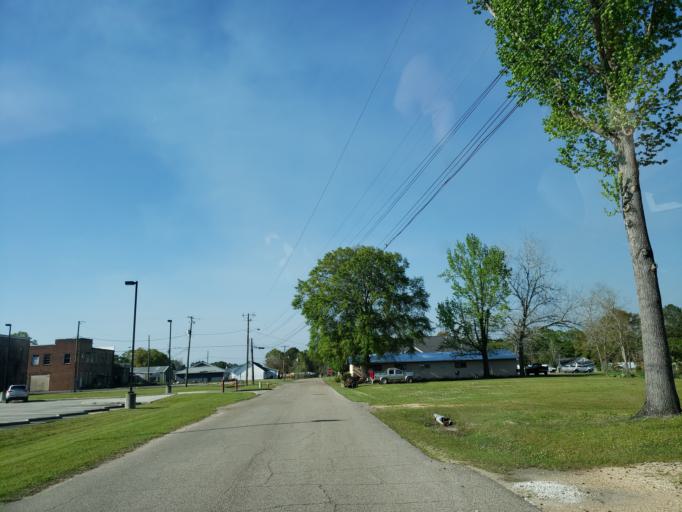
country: US
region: Mississippi
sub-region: Perry County
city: Richton
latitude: 31.3480
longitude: -88.9351
